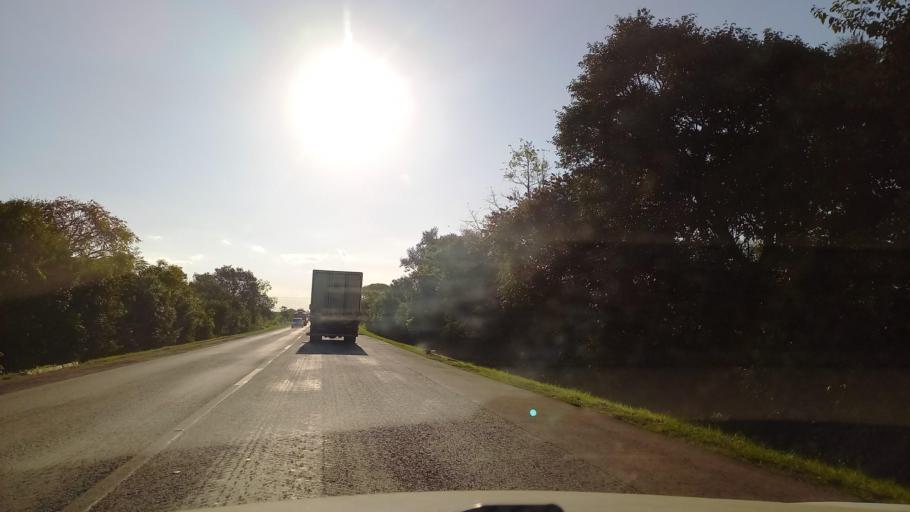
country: BR
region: Rio Grande do Sul
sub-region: Venancio Aires
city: Venancio Aires
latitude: -29.6735
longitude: -52.0184
